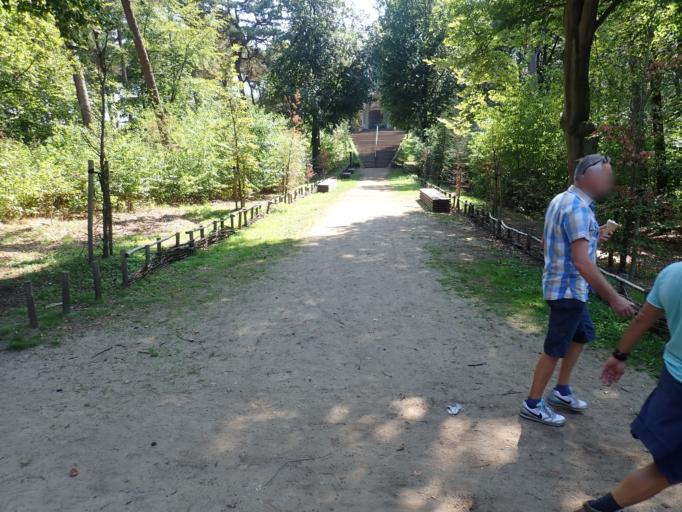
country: BE
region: Flanders
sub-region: Provincie Vlaams-Brabant
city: Scherpenheuvel-Zichem
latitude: 51.0302
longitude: 4.9828
